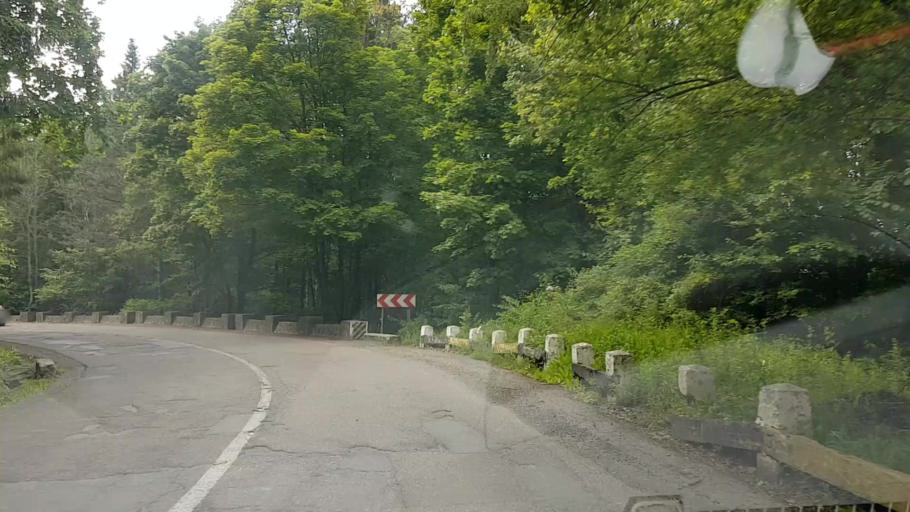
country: RO
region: Neamt
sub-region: Comuna Bicaz
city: Dodeni
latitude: 46.9393
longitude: 26.1162
